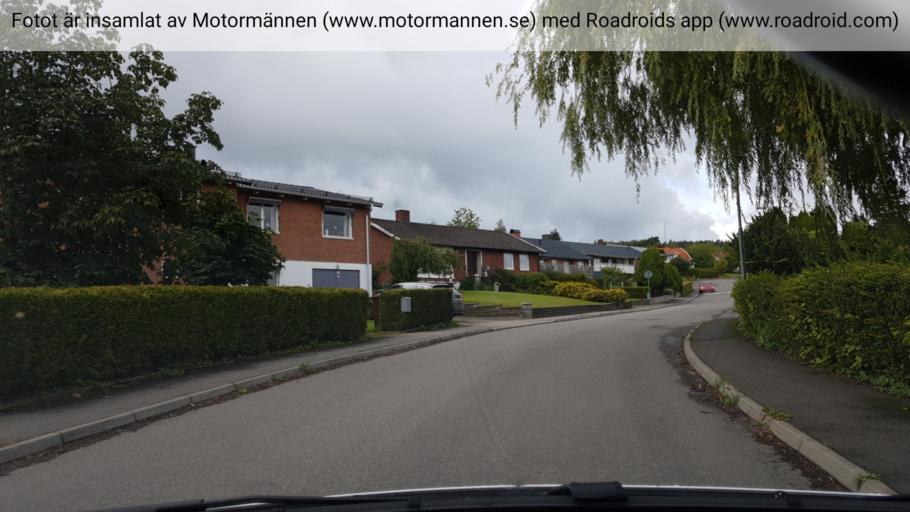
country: SE
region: Vaestra Goetaland
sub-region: Skovde Kommun
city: Skoevde
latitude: 58.3902
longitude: 13.8265
